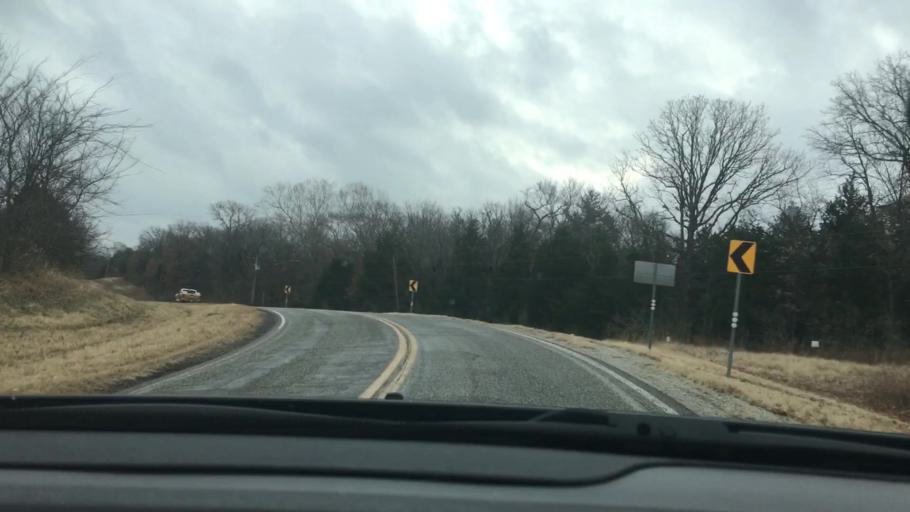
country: US
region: Oklahoma
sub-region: Johnston County
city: Tishomingo
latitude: 34.2089
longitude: -96.6356
